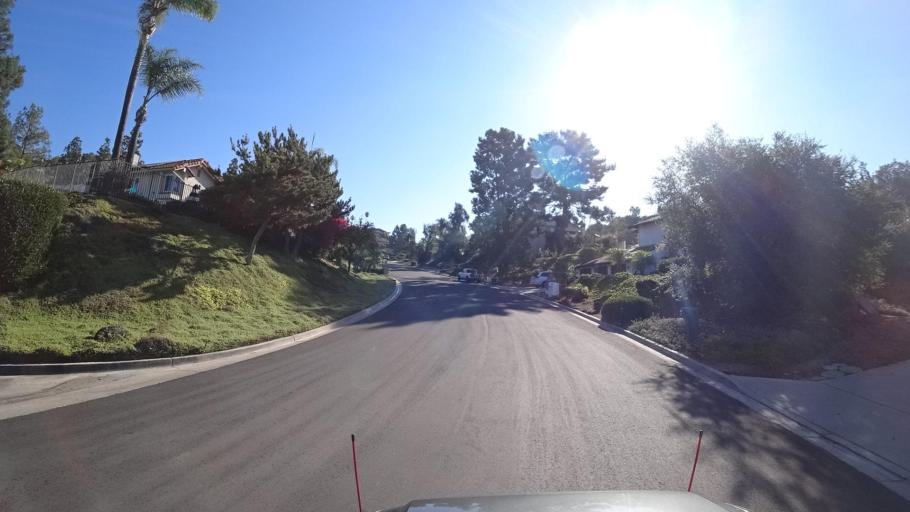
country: US
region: California
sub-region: San Diego County
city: Spring Valley
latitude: 32.7630
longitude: -116.9904
